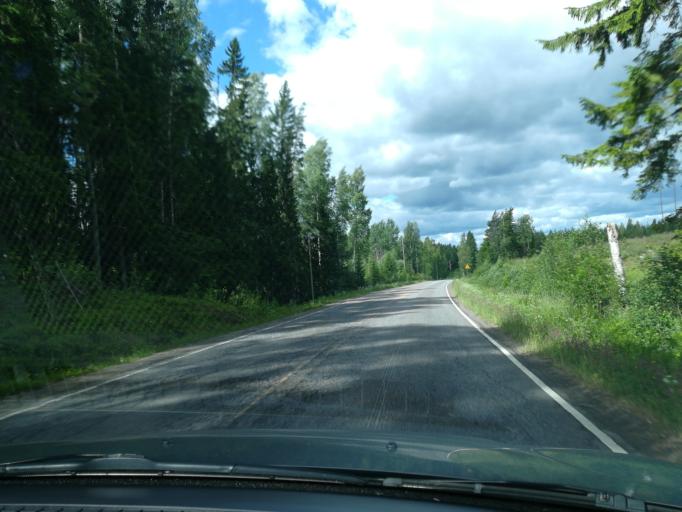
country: FI
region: Southern Savonia
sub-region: Mikkeli
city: Maentyharju
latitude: 61.3615
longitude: 27.0671
